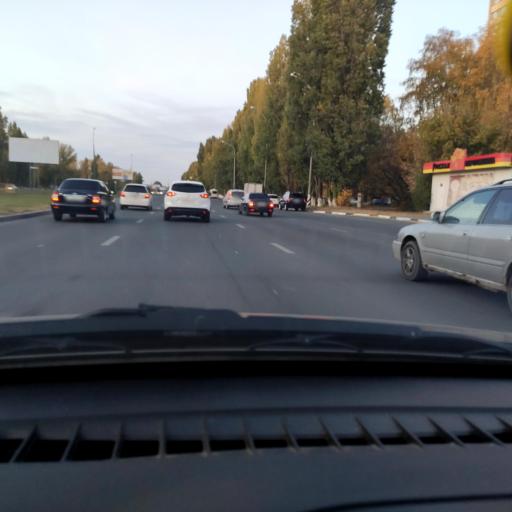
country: RU
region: Samara
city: Tol'yatti
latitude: 53.5093
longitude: 49.2771
